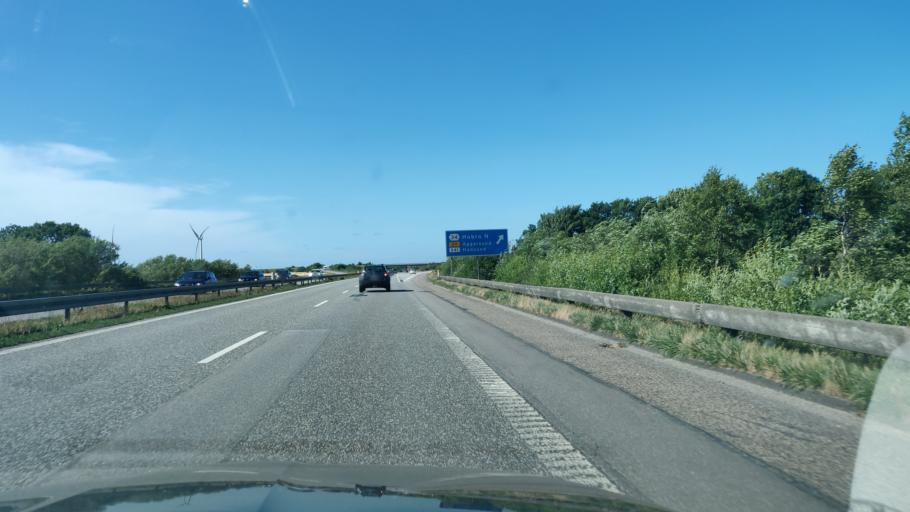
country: DK
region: North Denmark
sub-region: Mariagerfjord Kommune
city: Hobro
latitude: 56.6621
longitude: 9.7351
